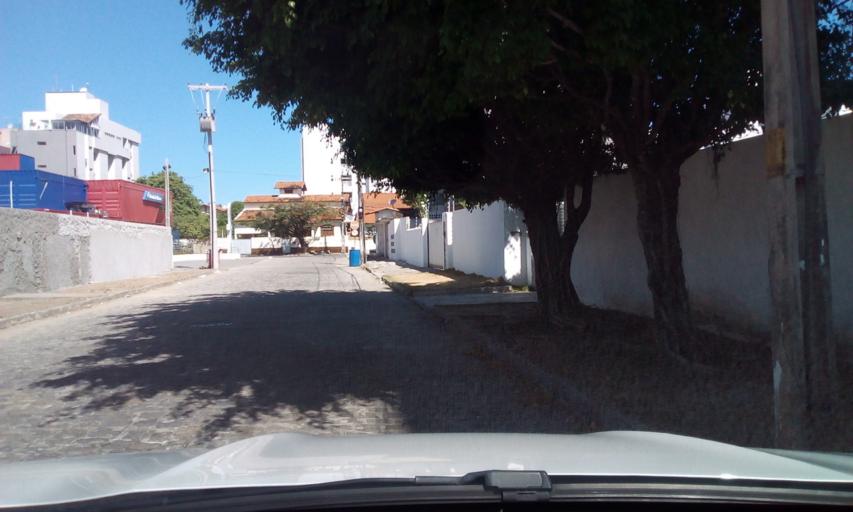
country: BR
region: Paraiba
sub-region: Joao Pessoa
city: Joao Pessoa
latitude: -7.0886
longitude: -34.8359
